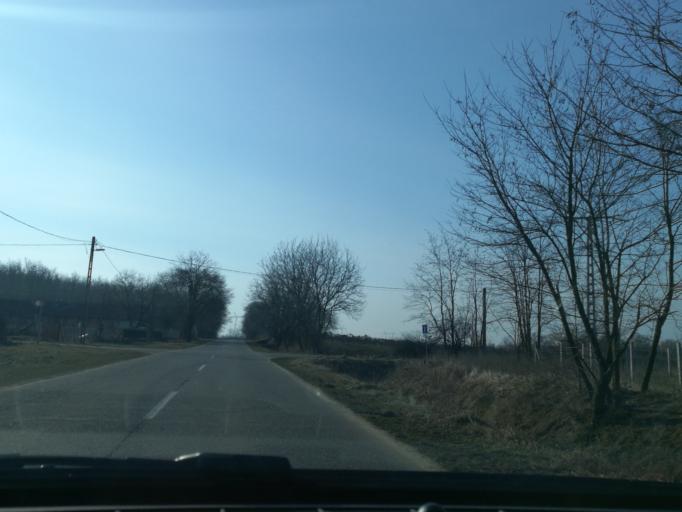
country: HU
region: Szabolcs-Szatmar-Bereg
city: Levelek
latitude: 47.9851
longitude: 21.9693
